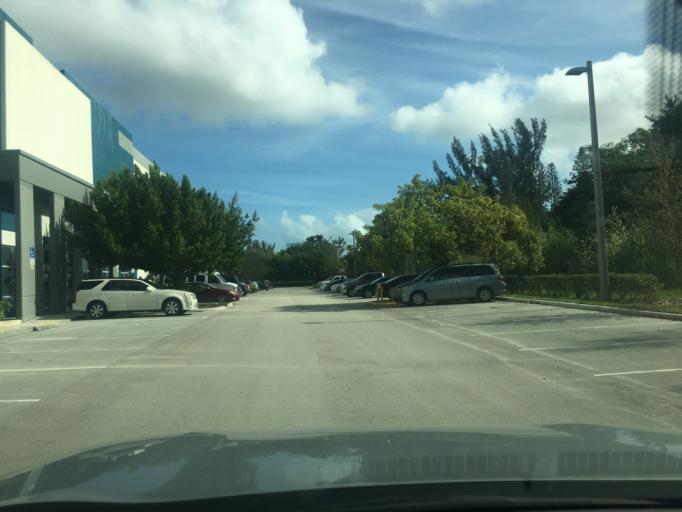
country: US
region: Florida
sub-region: Broward County
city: Broadview Park
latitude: 26.0800
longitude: -80.1788
